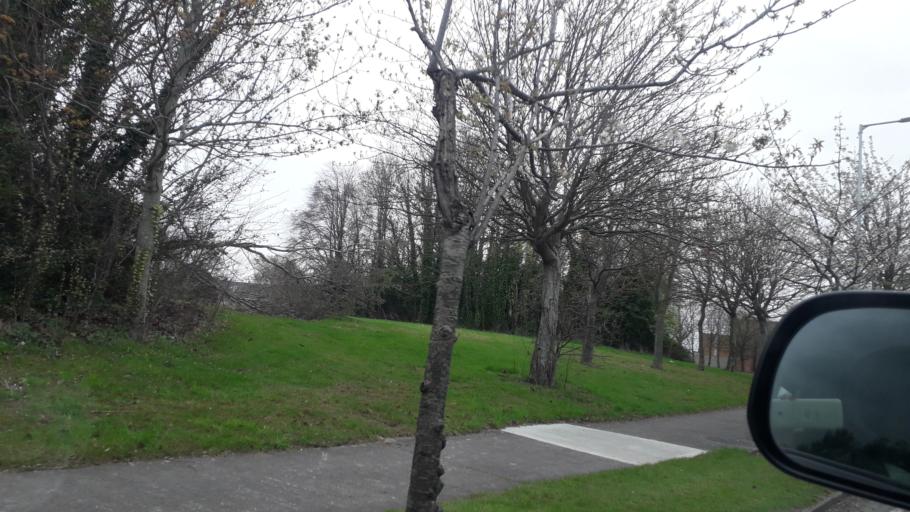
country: IE
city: Bonnybrook
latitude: 53.3991
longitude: -6.2203
